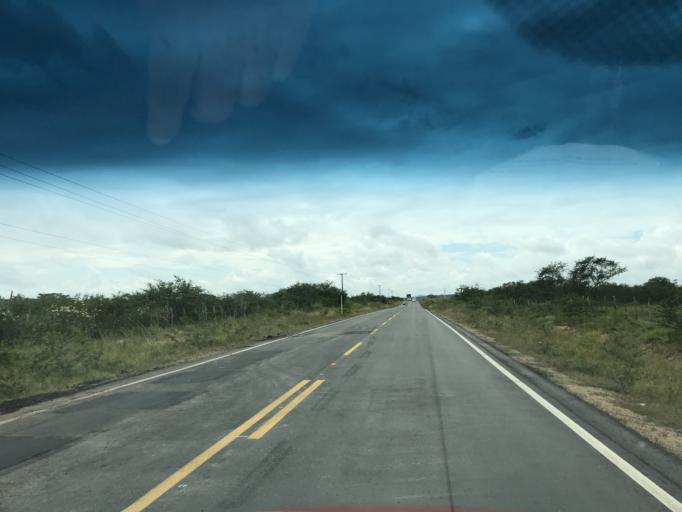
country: BR
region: Bahia
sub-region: Castro Alves
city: Castro Alves
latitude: -12.6835
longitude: -39.3071
